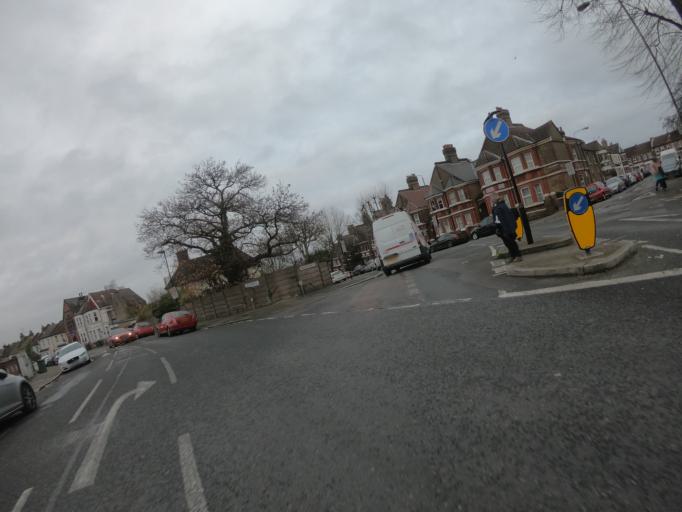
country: GB
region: England
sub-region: Greater London
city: Woolwich
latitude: 51.4838
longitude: 0.0829
